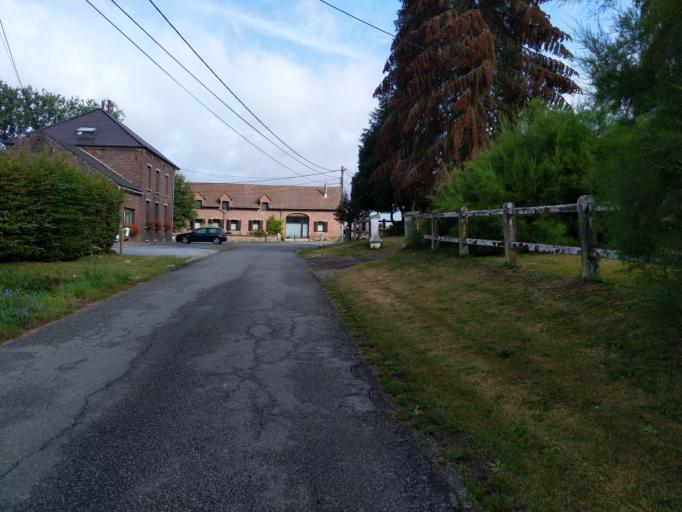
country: BE
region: Wallonia
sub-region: Province du Hainaut
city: Jurbise
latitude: 50.5343
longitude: 3.8831
